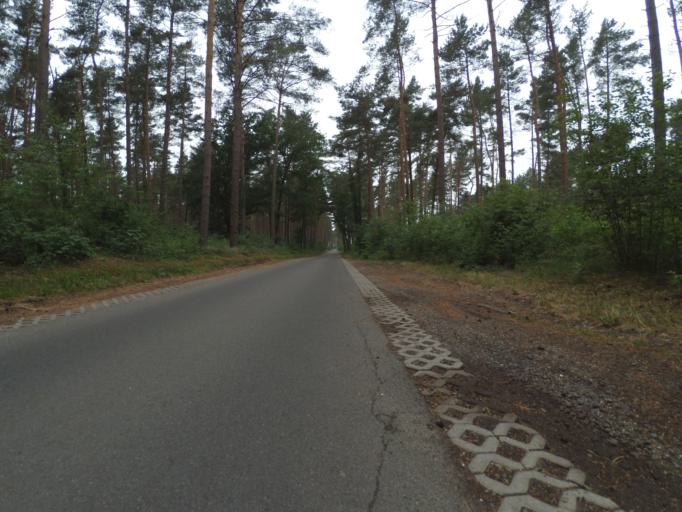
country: DE
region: Mecklenburg-Vorpommern
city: Plau am See
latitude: 53.4811
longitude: 12.2766
